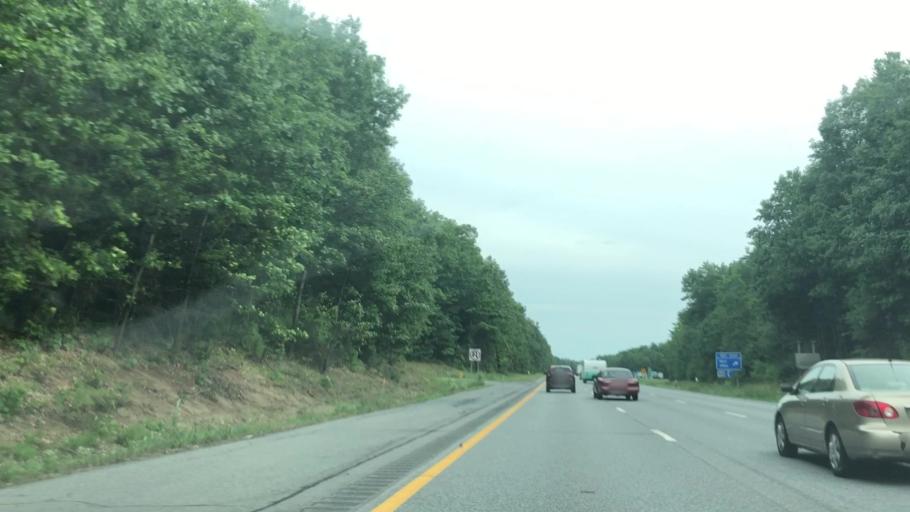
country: US
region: New York
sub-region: Warren County
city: West Glens Falls
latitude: 43.2800
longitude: -73.6794
